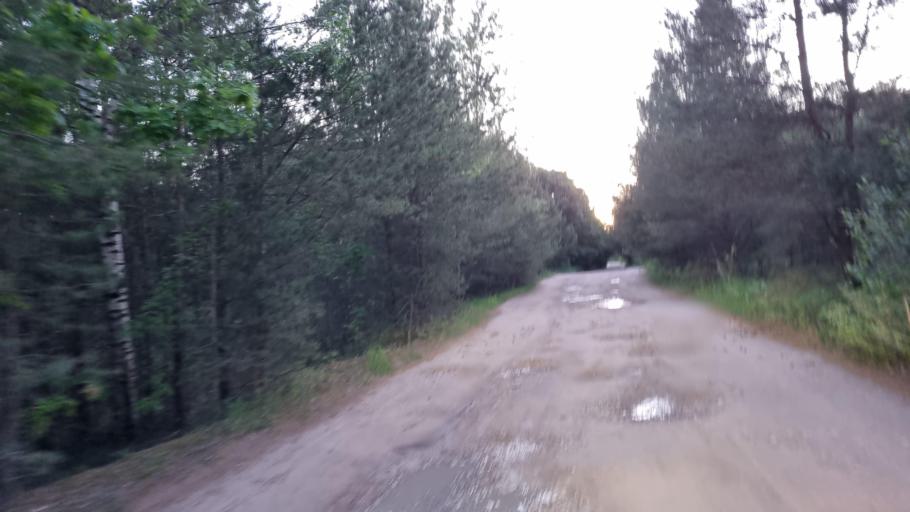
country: LV
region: Riga
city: Daugavgriva
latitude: 57.0219
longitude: 24.0313
